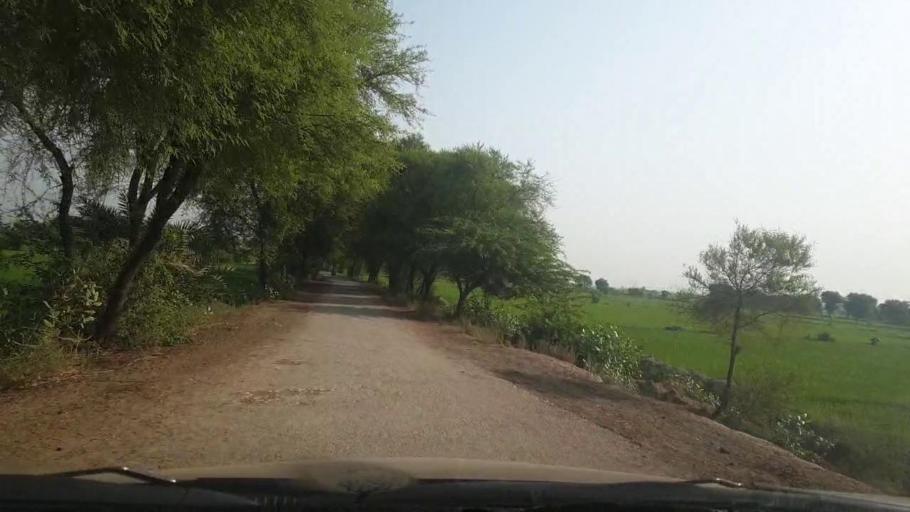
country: PK
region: Sindh
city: Larkana
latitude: 27.5867
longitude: 68.1607
